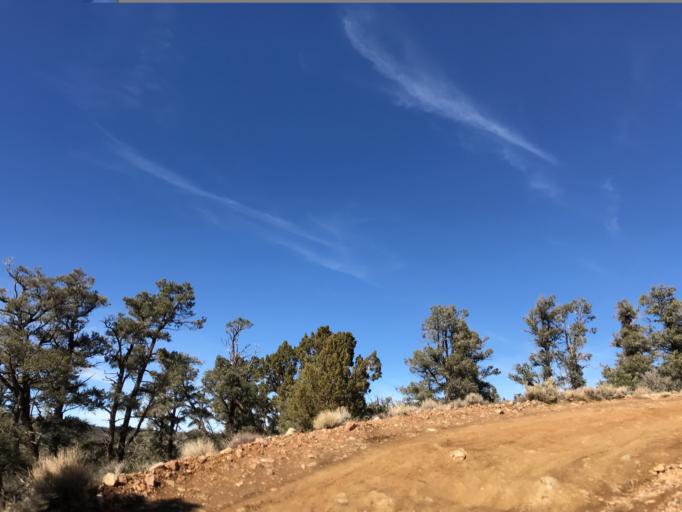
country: US
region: California
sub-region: San Bernardino County
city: Big Bear City
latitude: 34.2548
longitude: -116.7383
